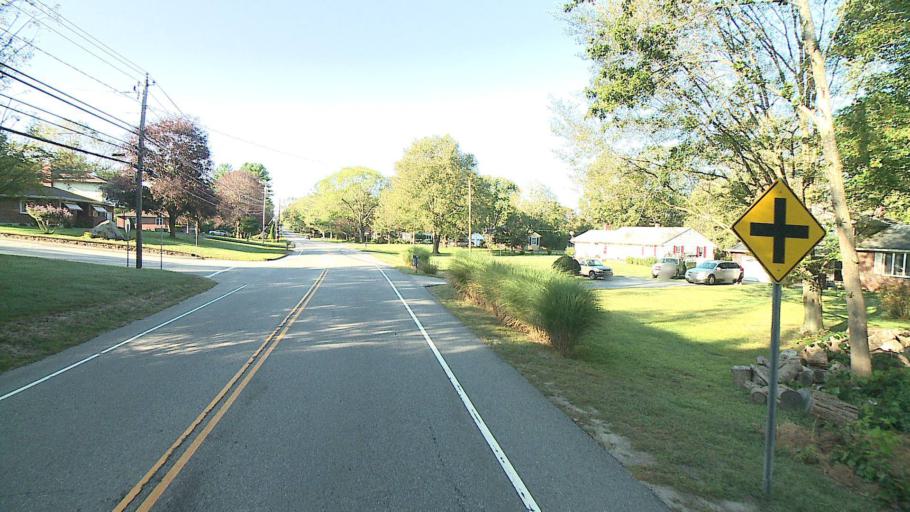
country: US
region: Connecticut
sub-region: Windham County
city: East Brooklyn
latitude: 41.7789
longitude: -71.8936
